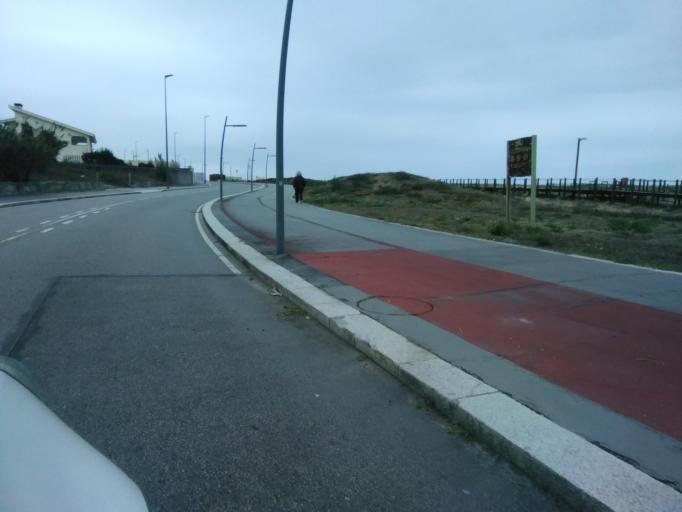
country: PT
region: Porto
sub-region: Matosinhos
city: Lavra
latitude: 41.2584
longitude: -8.7233
